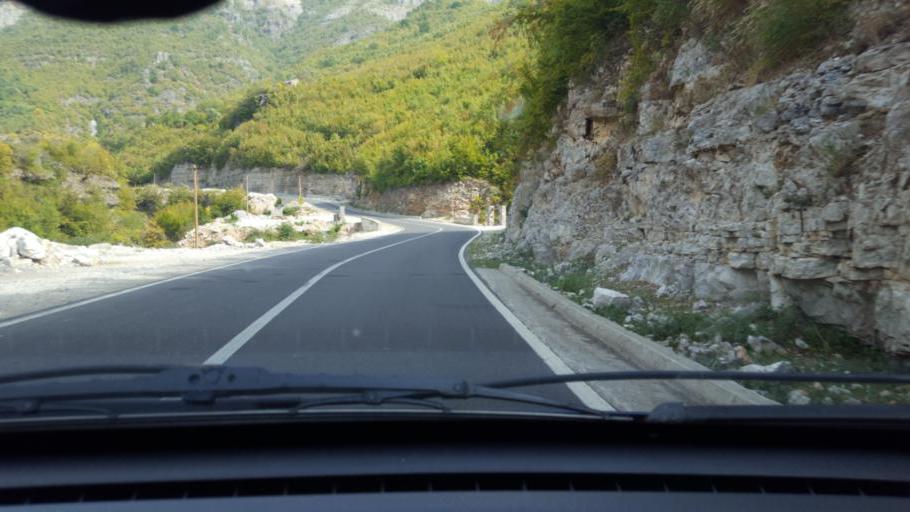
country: AL
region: Shkoder
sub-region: Rrethi i Malesia e Madhe
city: Kastrat
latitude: 42.4263
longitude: 19.5262
